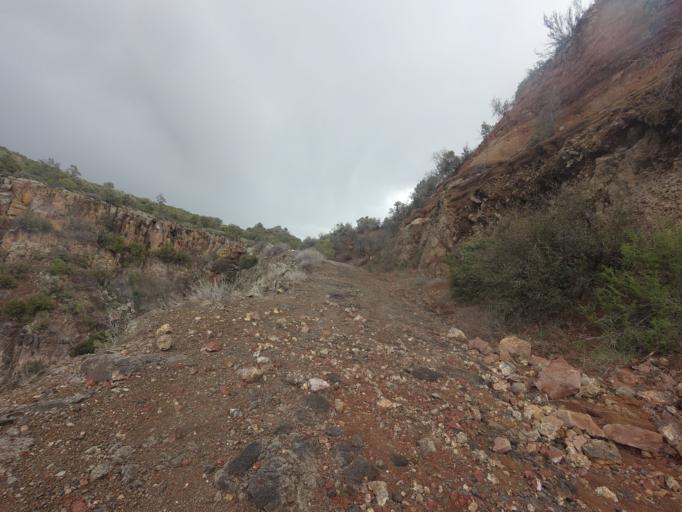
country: US
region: Arizona
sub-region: Gila County
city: Pine
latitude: 34.4080
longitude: -111.5784
